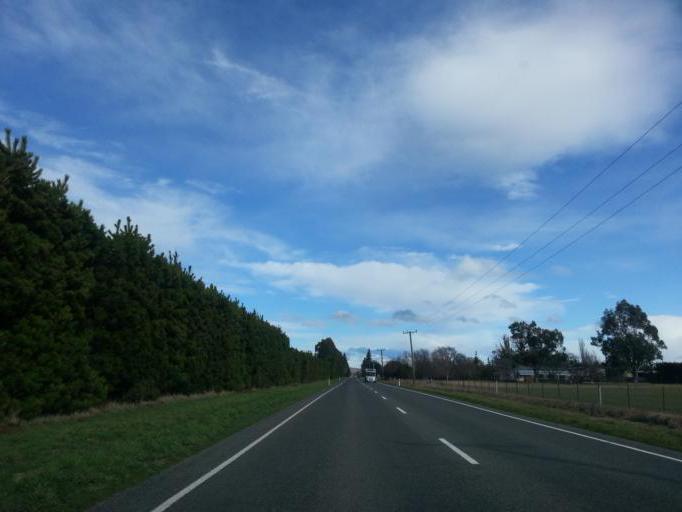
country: NZ
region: Canterbury
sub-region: Hurunui District
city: Amberley
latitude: -42.7857
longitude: 172.8388
